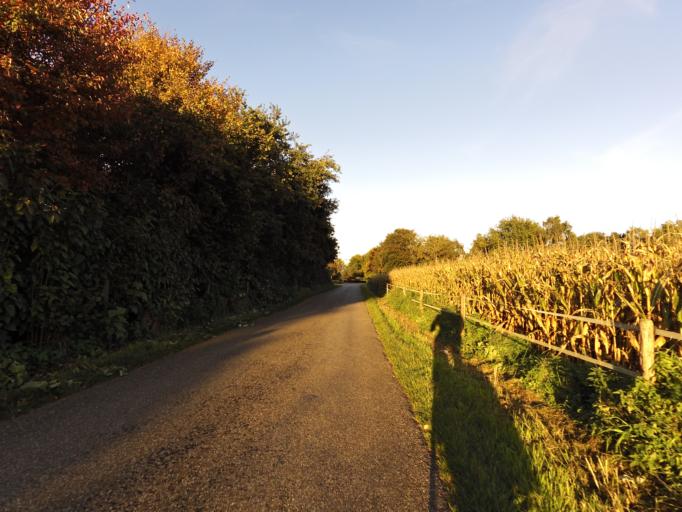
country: NL
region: Gelderland
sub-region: Gemeente Doesburg
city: Doesburg
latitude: 51.9451
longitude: 6.1458
